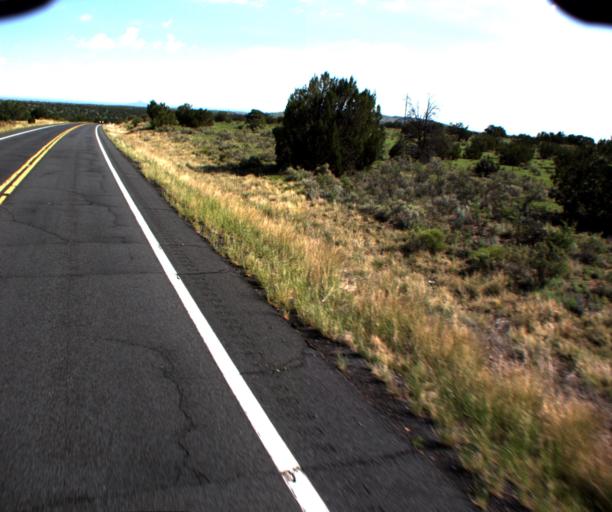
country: US
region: Arizona
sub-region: Coconino County
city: Williams
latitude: 35.5072
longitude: -112.1734
